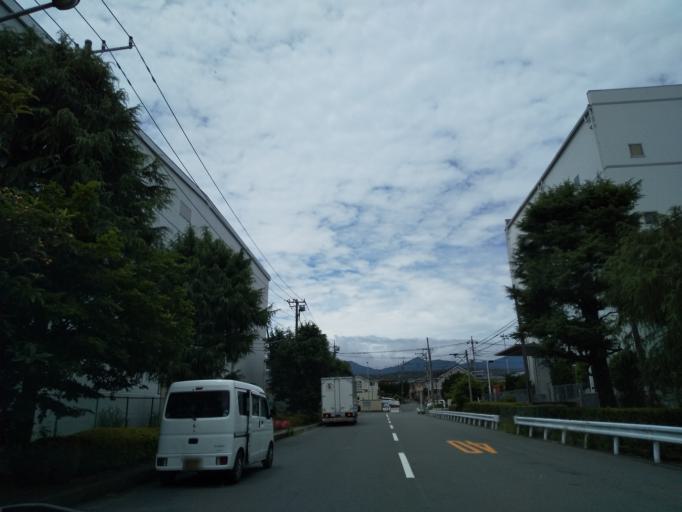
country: JP
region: Kanagawa
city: Zama
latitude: 35.5194
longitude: 139.3401
